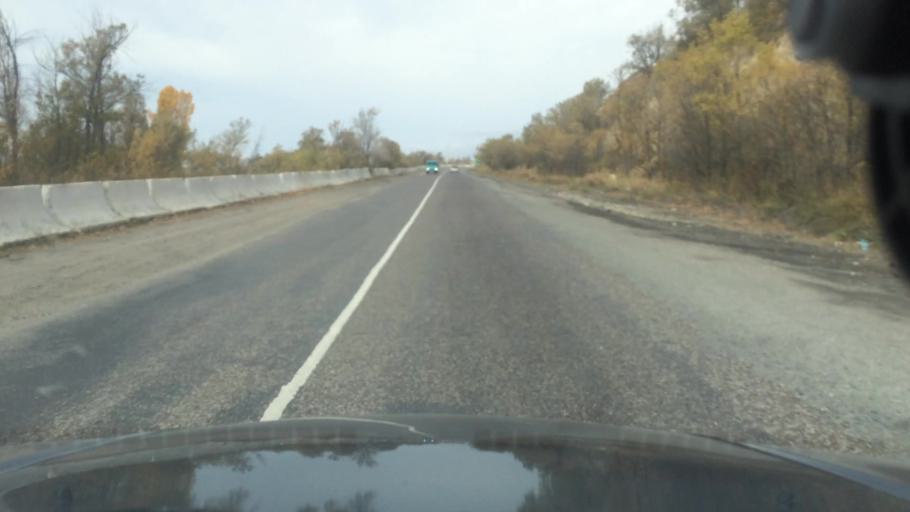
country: KG
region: Ysyk-Koel
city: Karakol
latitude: 42.5964
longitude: 78.3797
